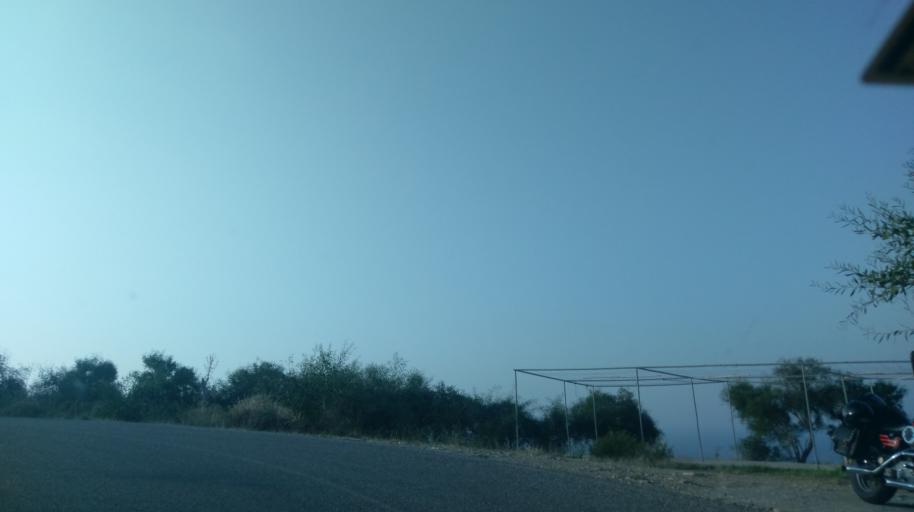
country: CY
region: Ammochostos
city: Trikomo
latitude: 35.4167
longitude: 33.9050
